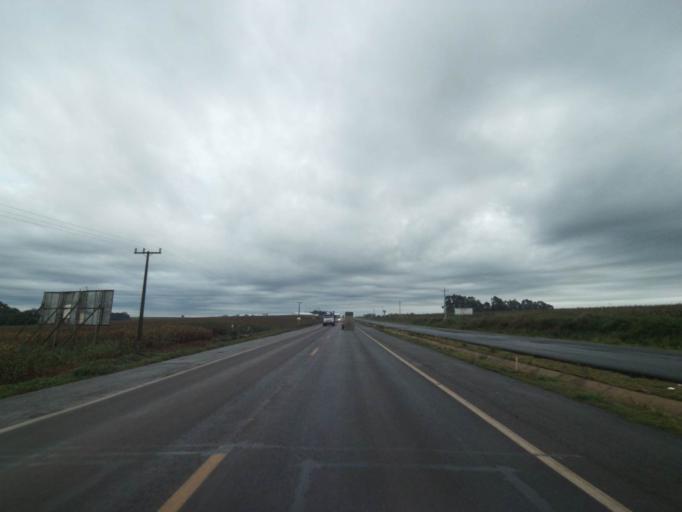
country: BR
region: Parana
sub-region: Toledo
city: Toledo
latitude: -24.6862
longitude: -53.7732
